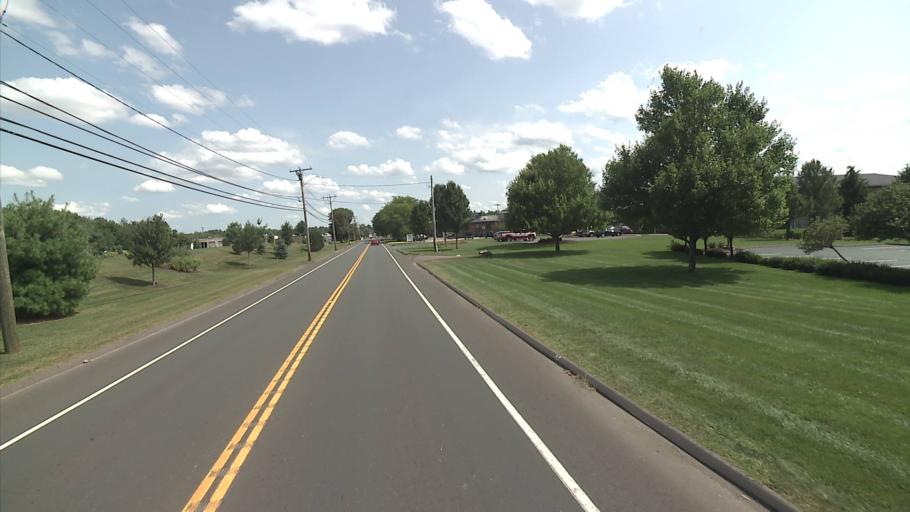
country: US
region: Connecticut
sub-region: Hartford County
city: South Windsor
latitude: 41.8527
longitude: -72.5845
